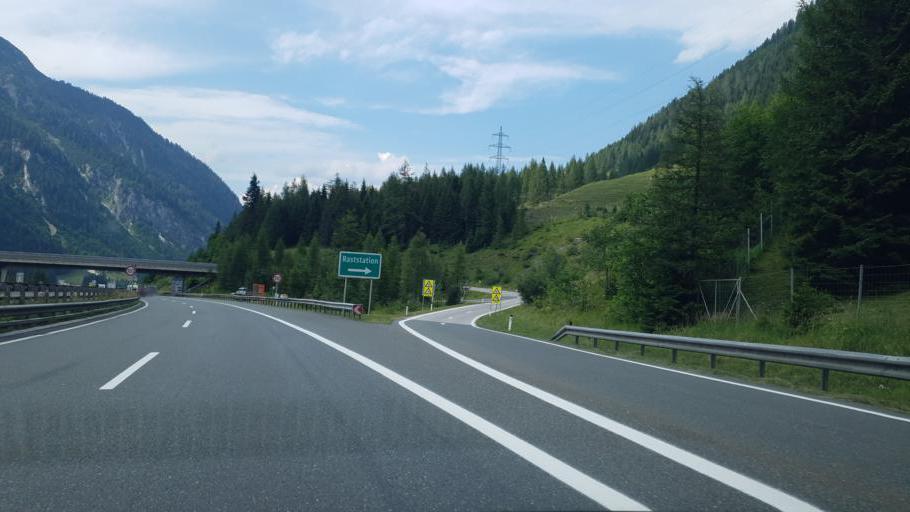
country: AT
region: Salzburg
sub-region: Politischer Bezirk Sankt Johann im Pongau
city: Untertauern
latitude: 47.2490
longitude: 13.4260
